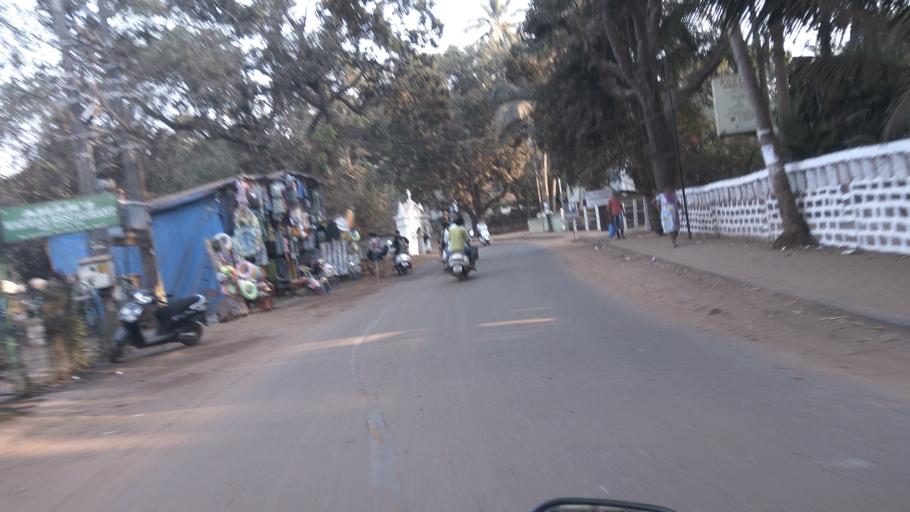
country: IN
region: Goa
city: Calangute
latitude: 15.5587
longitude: 73.7550
